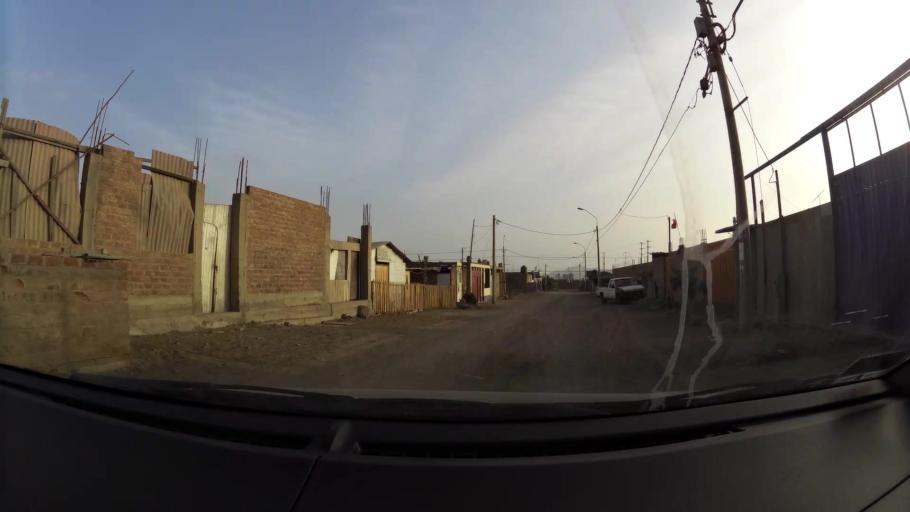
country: PE
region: Lima
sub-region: Lima
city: Santa Rosa
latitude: -11.7464
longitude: -77.1485
